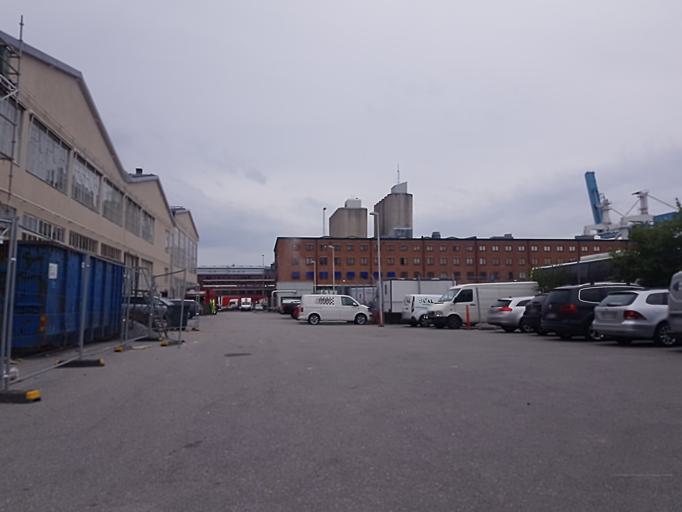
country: SE
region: Stockholm
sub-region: Lidingo
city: Lidingoe
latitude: 59.3400
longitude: 18.1232
